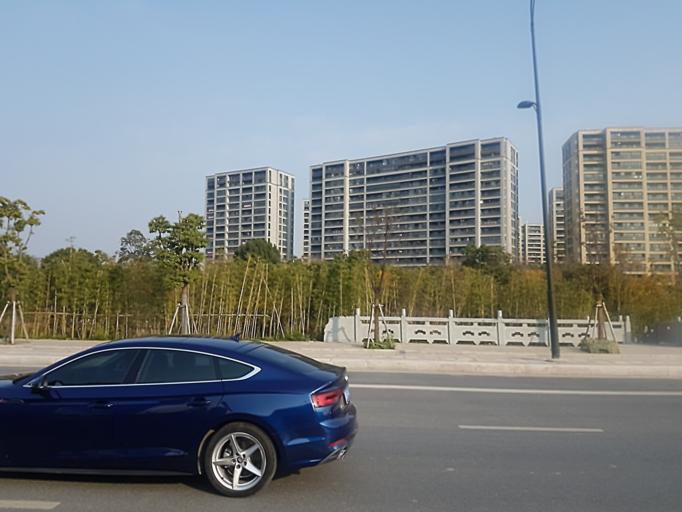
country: CN
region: Zhejiang Sheng
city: Jiangcun
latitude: 30.2982
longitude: 120.0533
